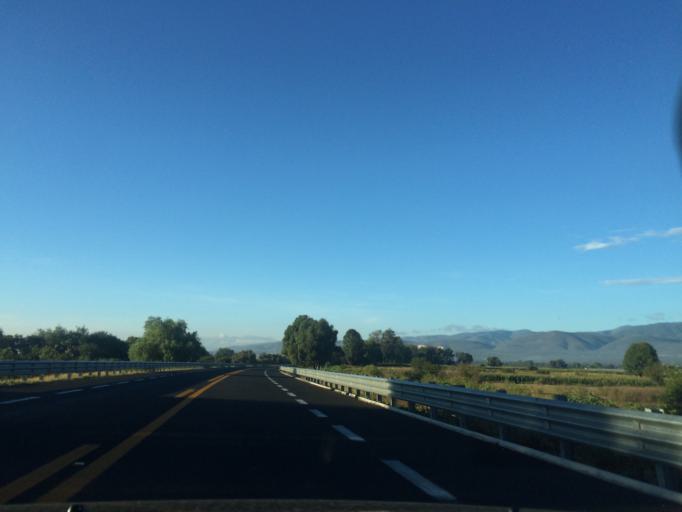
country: MX
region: Puebla
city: Santiago Miahuatlan
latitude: 18.5231
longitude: -97.4548
